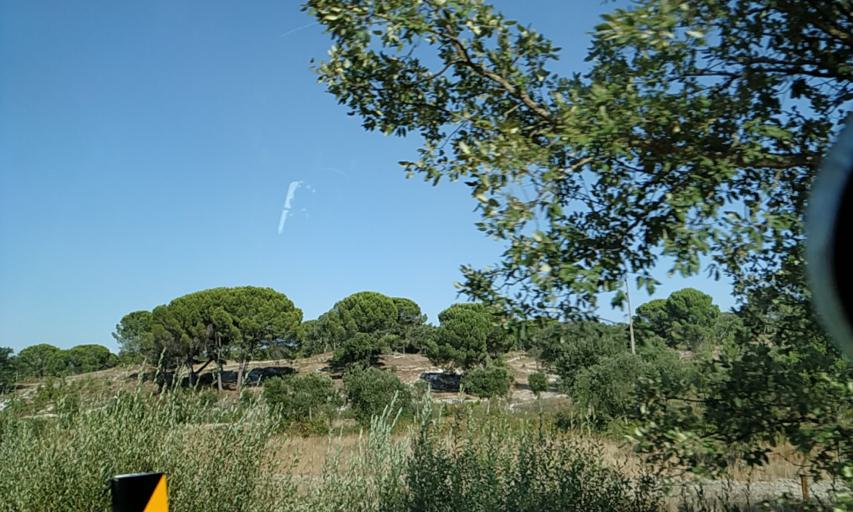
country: PT
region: Evora
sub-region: Vendas Novas
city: Vendas Novas
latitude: 38.7902
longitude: -8.5814
